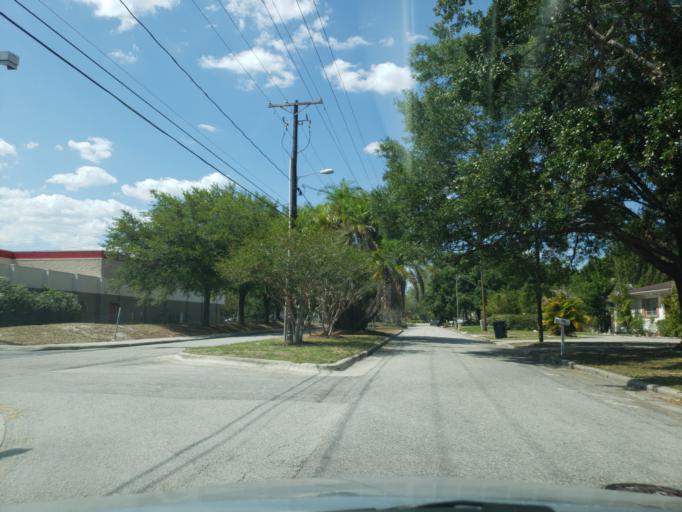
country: US
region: Florida
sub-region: Hillsborough County
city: Tampa
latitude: 27.9459
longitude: -82.5036
